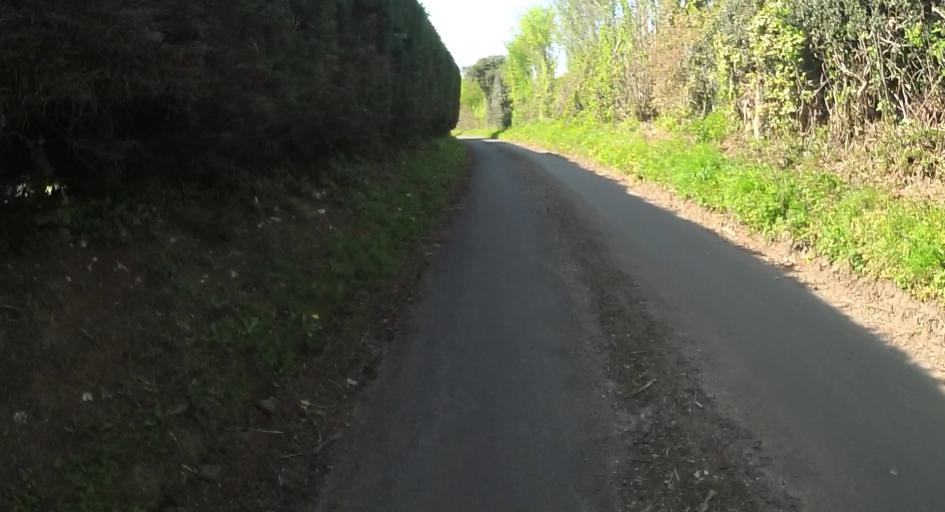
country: GB
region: England
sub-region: Hampshire
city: Alton
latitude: 51.1542
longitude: -1.0260
